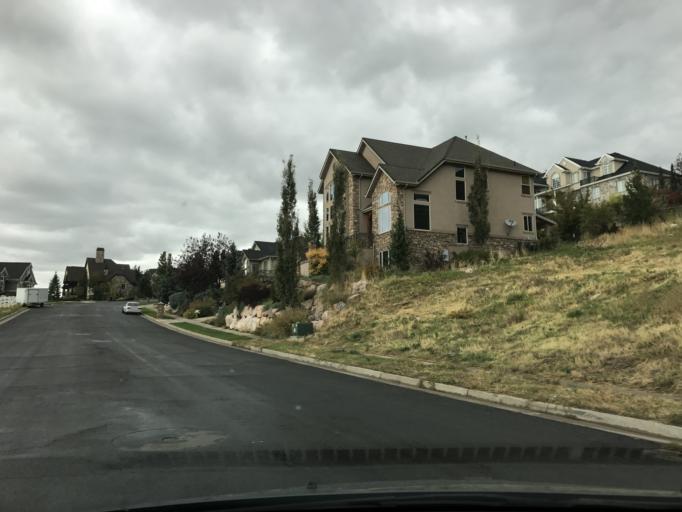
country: US
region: Utah
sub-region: Davis County
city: Fruit Heights
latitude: 41.0089
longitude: -111.8962
